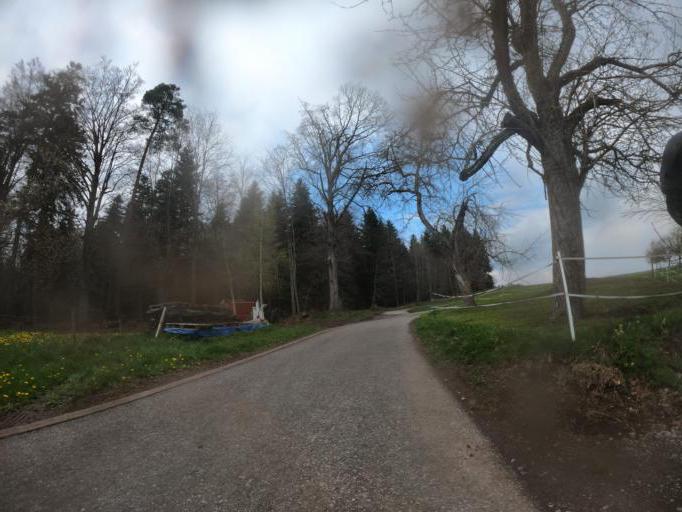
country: DE
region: Baden-Wuerttemberg
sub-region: Karlsruhe Region
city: Neuweiler
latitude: 48.6915
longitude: 8.5819
